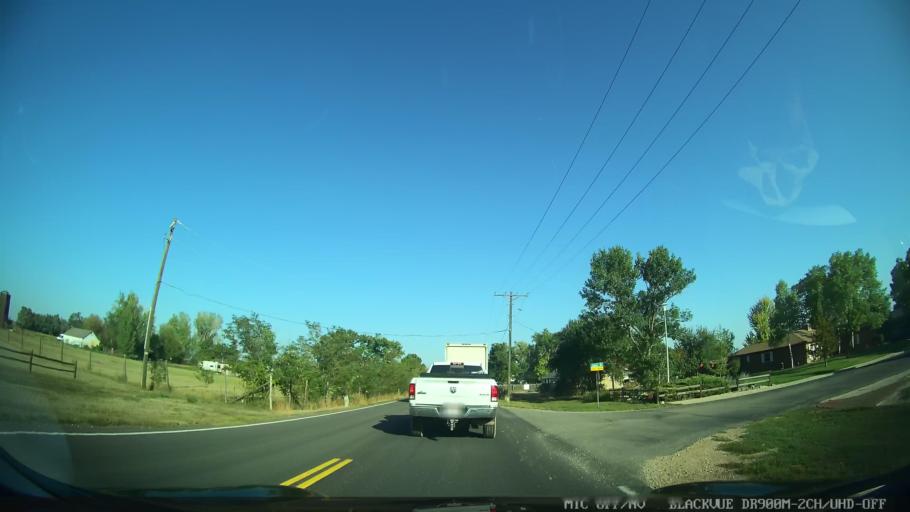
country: US
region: Colorado
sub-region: Larimer County
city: Loveland
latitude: 40.4510
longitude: -105.0605
